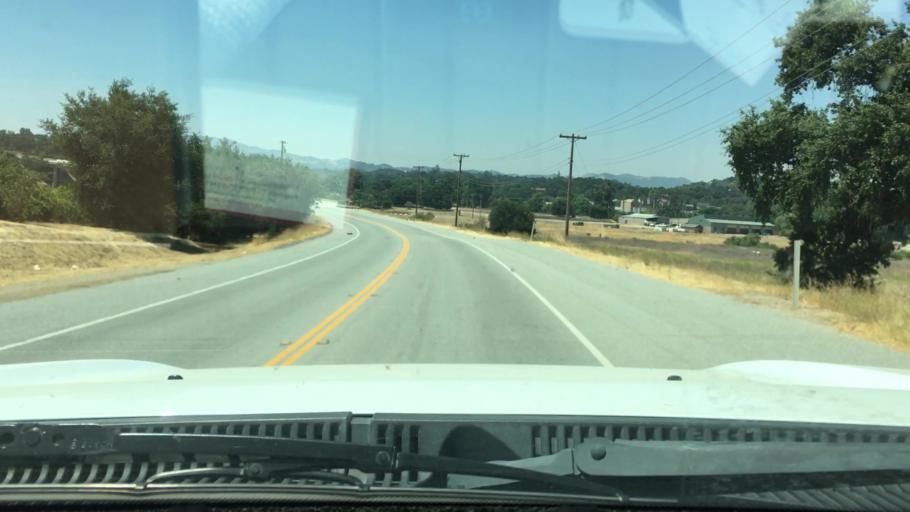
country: US
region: California
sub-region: San Luis Obispo County
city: Atascadero
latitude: 35.5031
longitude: -120.6558
